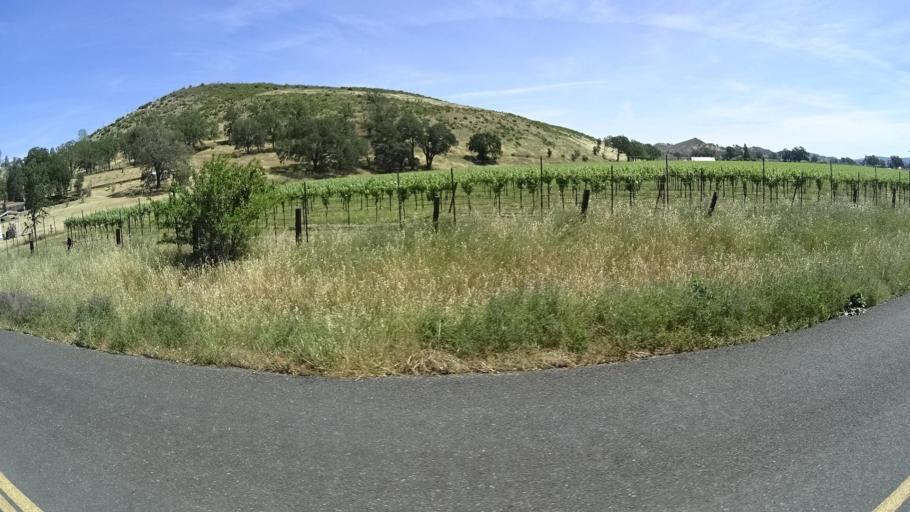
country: US
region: California
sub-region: Lake County
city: Middletown
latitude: 38.7653
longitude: -122.6193
